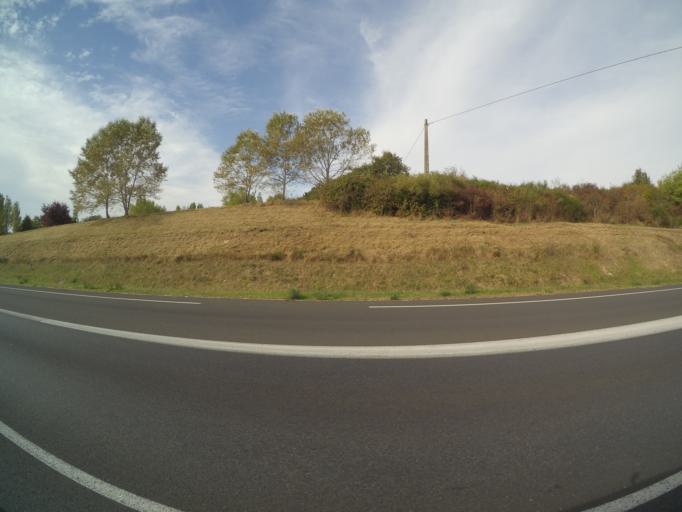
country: FR
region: Pays de la Loire
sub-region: Departement de Maine-et-Loire
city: Saumur
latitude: 47.2499
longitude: -0.1028
